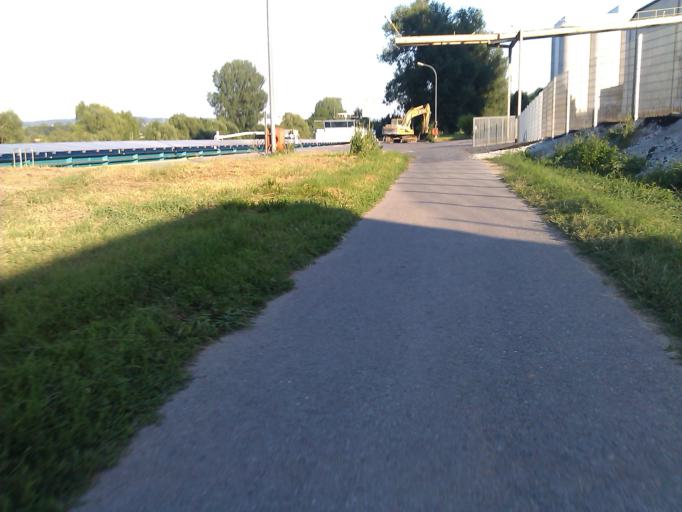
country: DE
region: Baden-Wuerttemberg
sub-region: Regierungsbezirk Stuttgart
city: Untereisesheim
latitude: 49.2289
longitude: 9.1935
